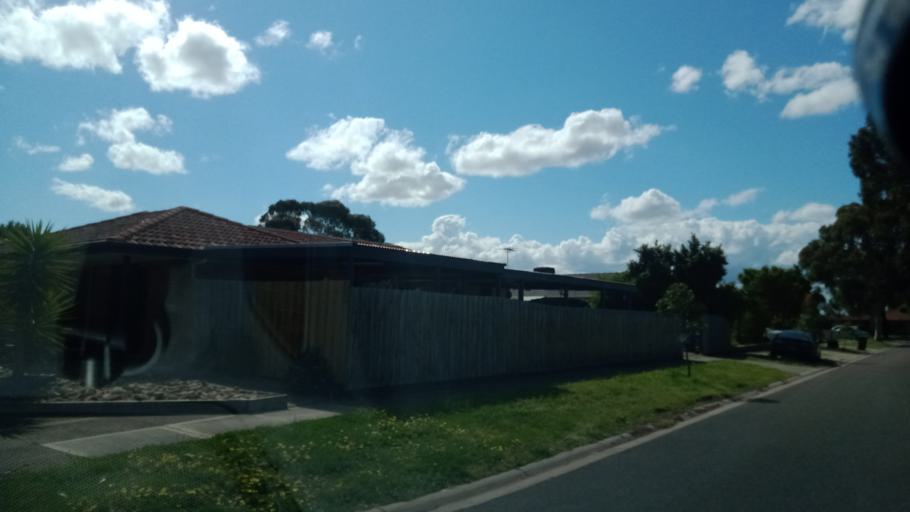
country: AU
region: Victoria
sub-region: Casey
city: Cranbourne West
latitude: -38.0984
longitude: 145.2590
